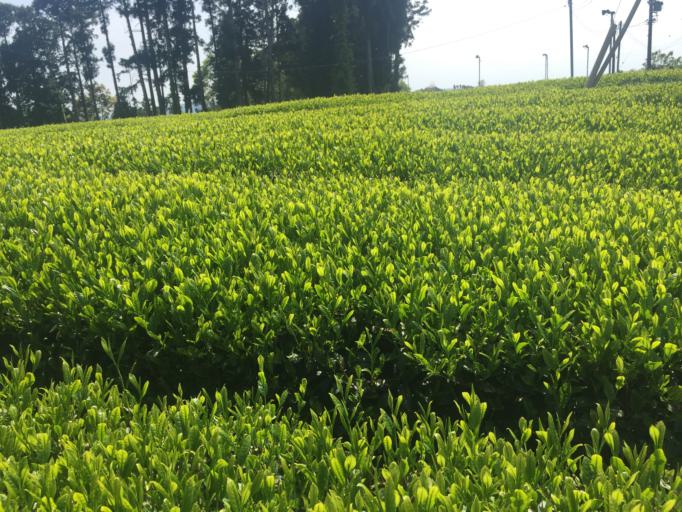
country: JP
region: Shizuoka
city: Kakegawa
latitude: 34.8192
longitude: 138.0405
